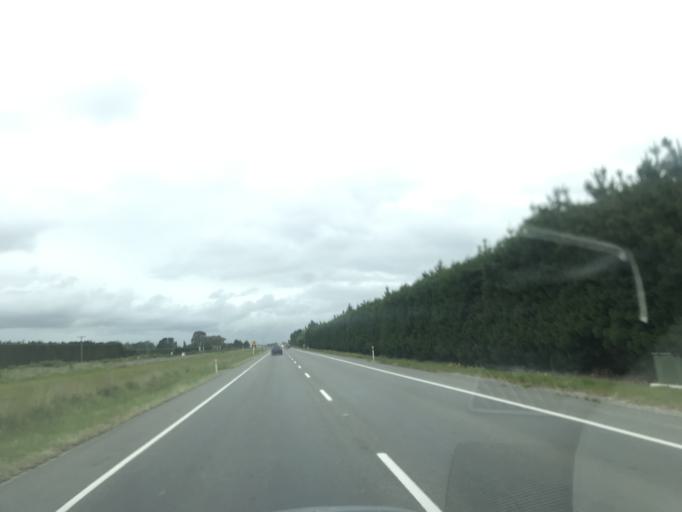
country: NZ
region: Canterbury
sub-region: Ashburton District
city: Tinwald
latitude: -43.9346
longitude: 171.6935
